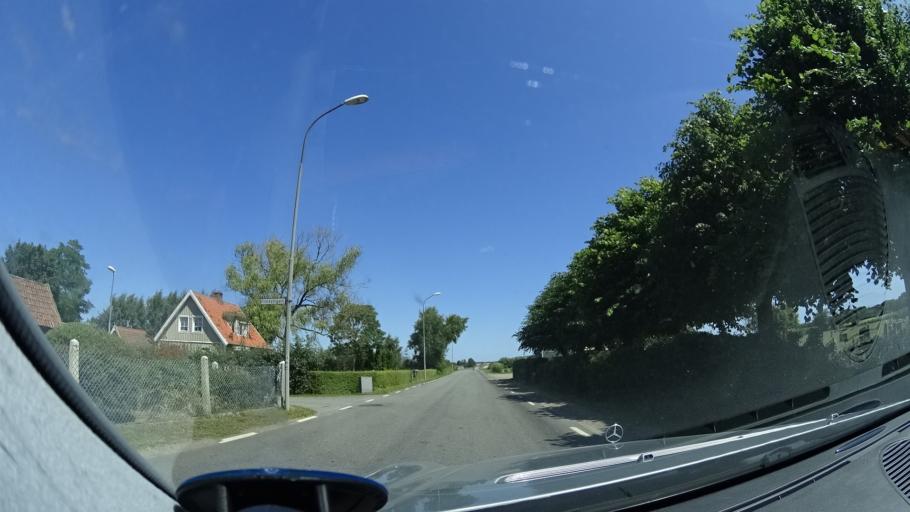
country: SE
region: Skane
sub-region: Kristianstads Kommun
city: Degeberga
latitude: 55.8845
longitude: 14.0207
